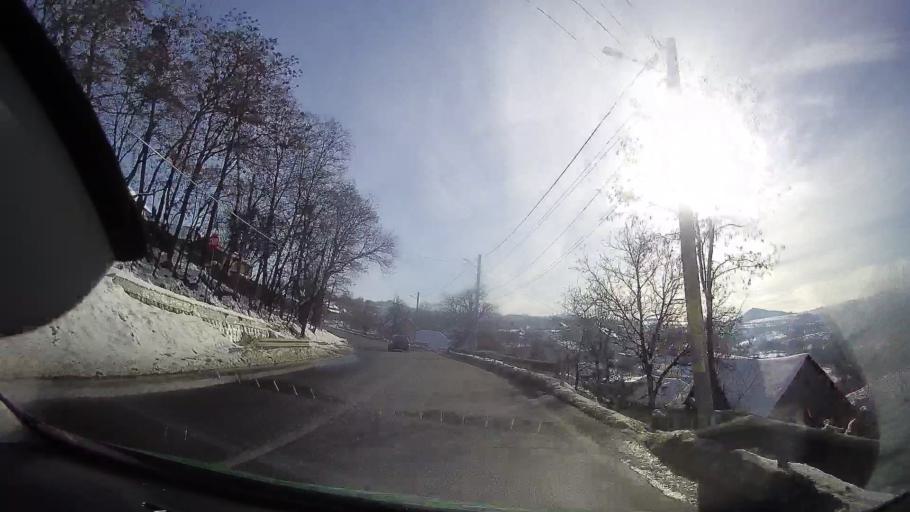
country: RO
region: Neamt
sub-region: Comuna Baltatesti
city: Baltatesti
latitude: 47.1155
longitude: 26.3127
